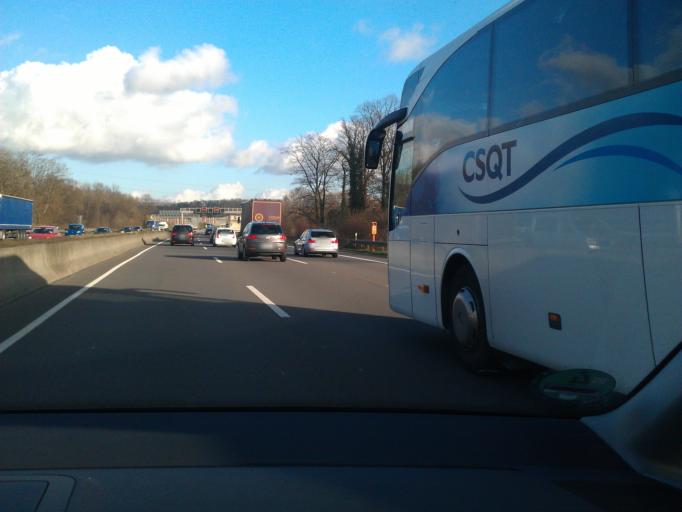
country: DE
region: North Rhine-Westphalia
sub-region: Regierungsbezirk Koln
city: Kerpen
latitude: 50.8995
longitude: 6.7050
